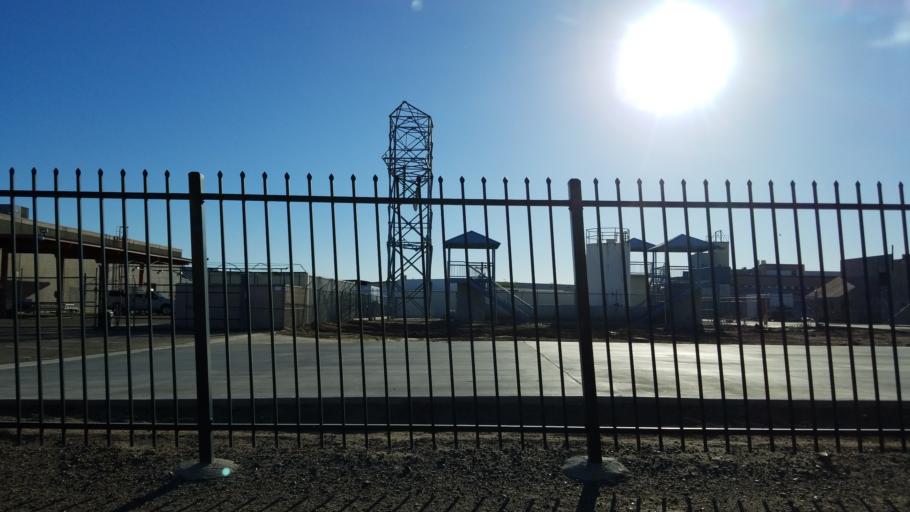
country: US
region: Arizona
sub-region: Maricopa County
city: Phoenix
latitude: 33.4253
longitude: -112.1063
